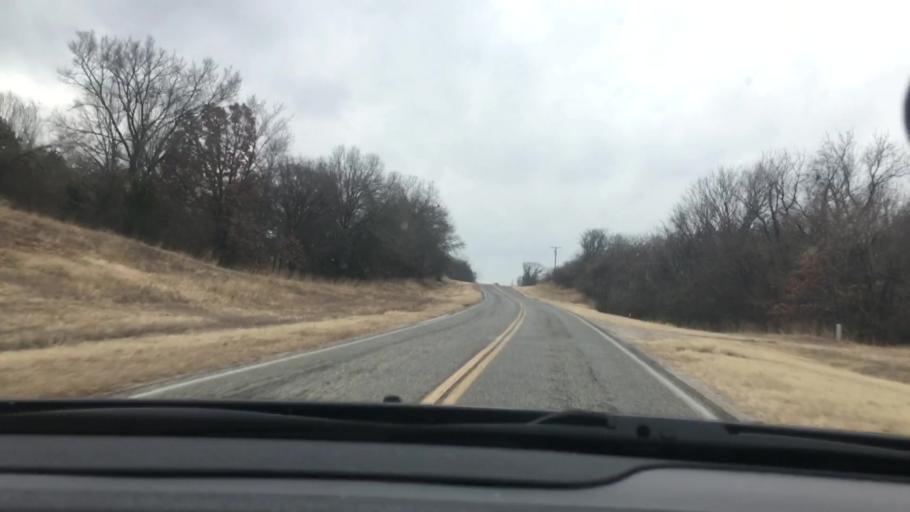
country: US
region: Oklahoma
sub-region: Johnston County
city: Tishomingo
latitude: 34.2244
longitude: -96.6361
